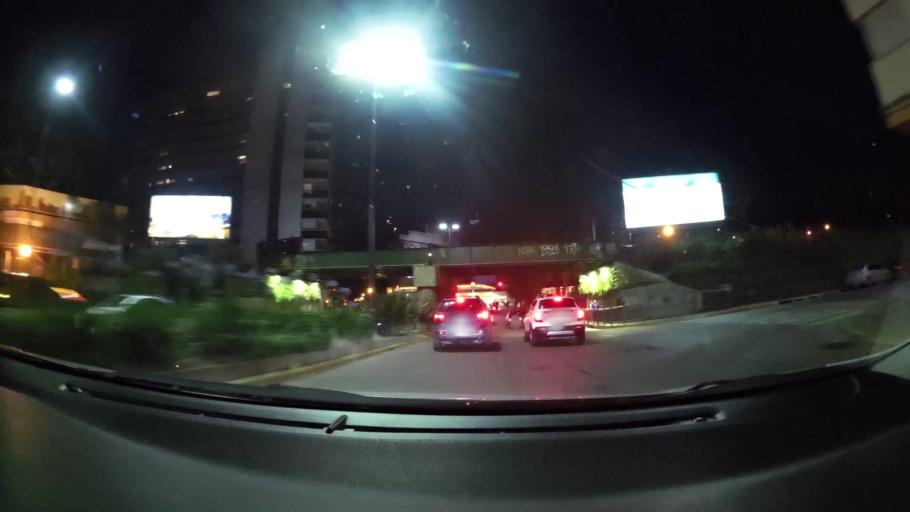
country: AR
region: Buenos Aires F.D.
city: Colegiales
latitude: -34.5698
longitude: -58.4578
